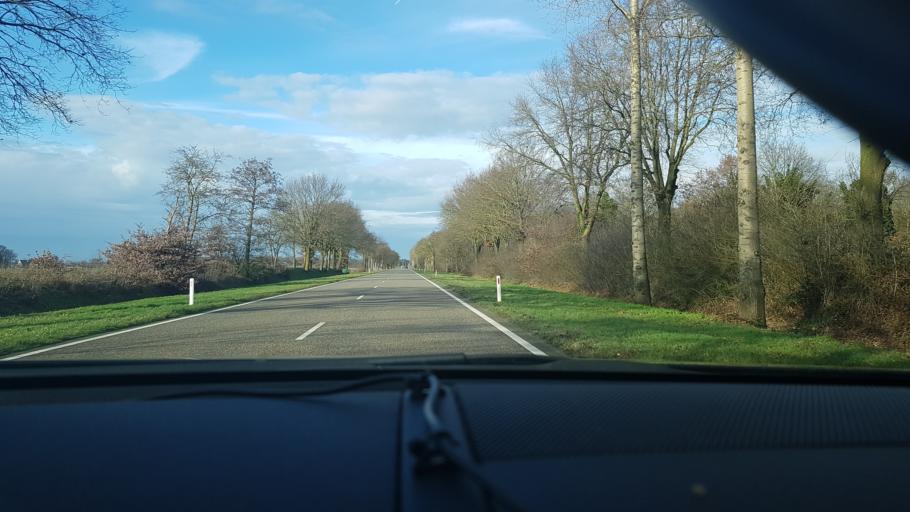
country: NL
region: Limburg
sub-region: Gemeente Peel en Maas
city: Maasbree
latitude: 51.3402
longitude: 6.0290
